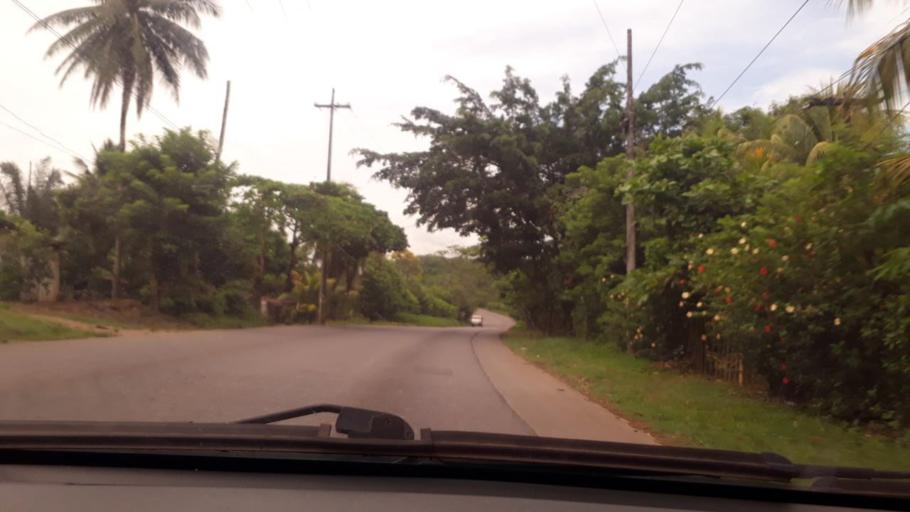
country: GT
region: Izabal
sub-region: Municipio de Puerto Barrios
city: Puerto Barrios
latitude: 15.6094
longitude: -88.5694
